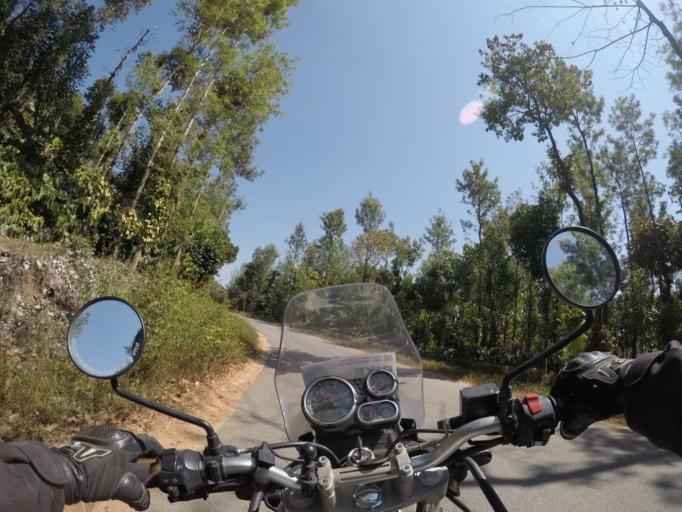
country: IN
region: Karnataka
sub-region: Chikmagalur
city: Mudigere
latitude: 13.0487
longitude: 75.6831
